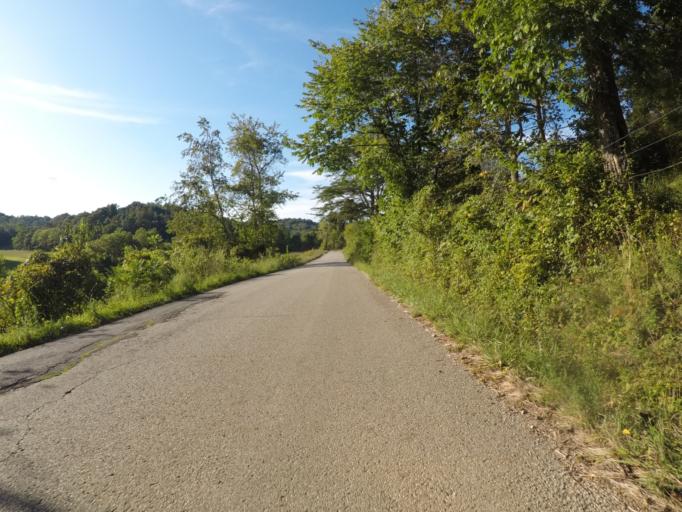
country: US
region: West Virginia
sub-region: Cabell County
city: Huntington
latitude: 38.5154
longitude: -82.5002
